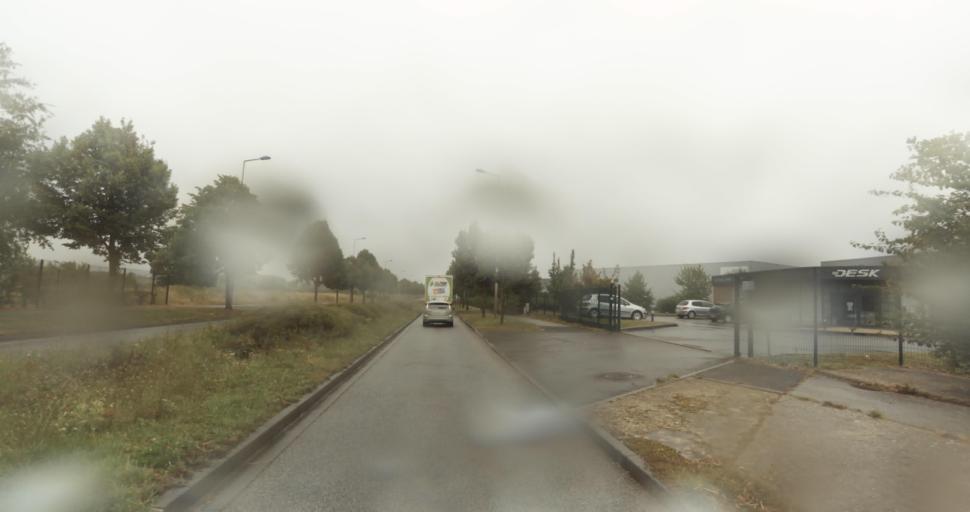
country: FR
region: Haute-Normandie
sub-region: Departement de l'Eure
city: Evreux
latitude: 49.0132
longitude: 1.1866
